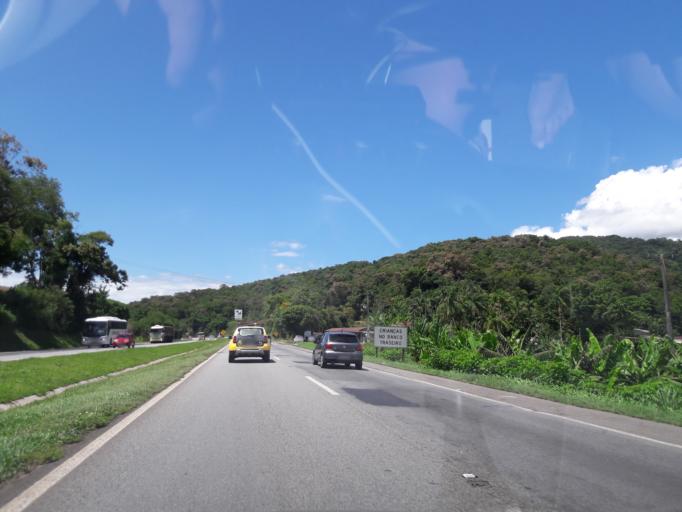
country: BR
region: Parana
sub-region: Antonina
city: Antonina
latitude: -25.5445
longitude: -48.7798
